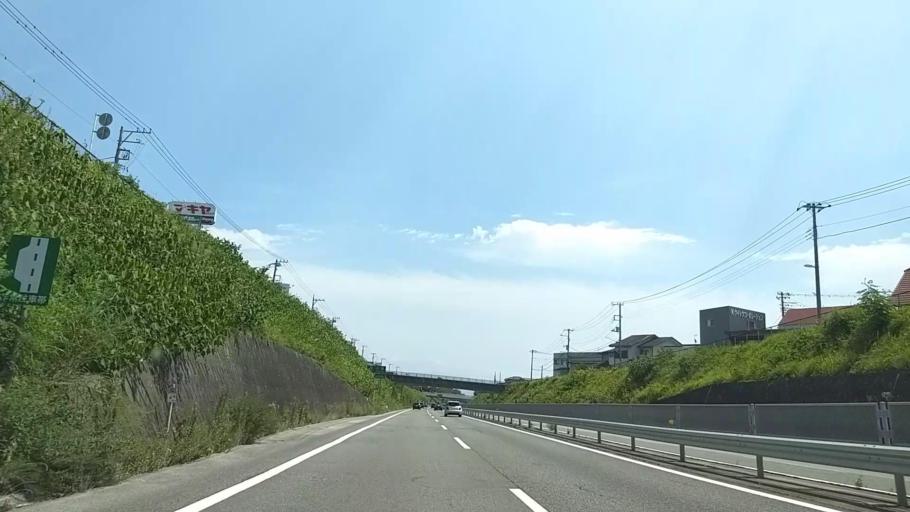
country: JP
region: Shizuoka
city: Fuji
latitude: 35.1913
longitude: 138.6723
